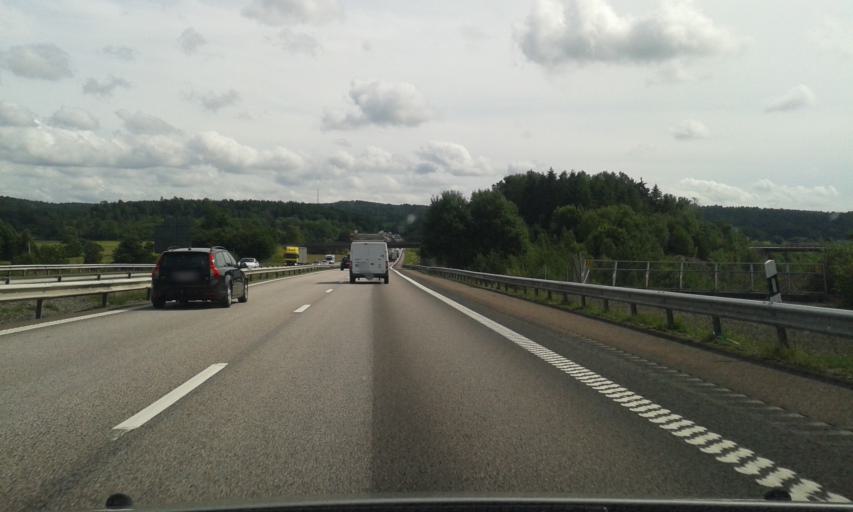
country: SE
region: Halland
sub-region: Kungsbacka Kommun
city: Fjaeras kyrkby
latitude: 57.4219
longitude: 12.1658
